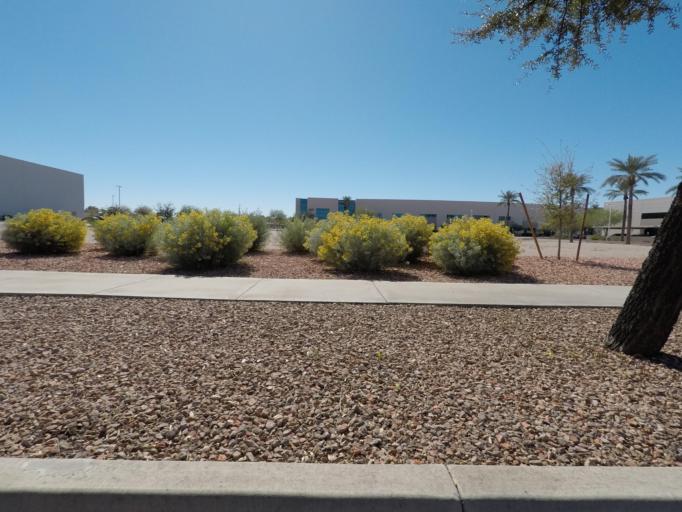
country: US
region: Arizona
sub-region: Maricopa County
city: Guadalupe
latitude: 33.4020
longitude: -111.9889
